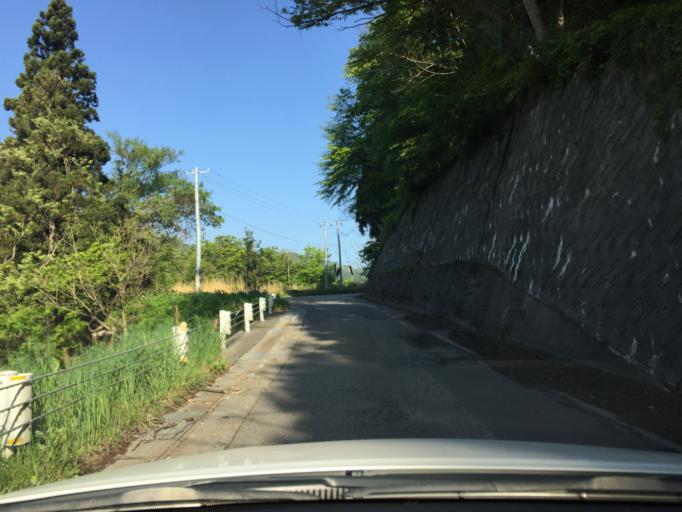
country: JP
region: Fukushima
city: Kitakata
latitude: 37.6662
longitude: 139.7476
